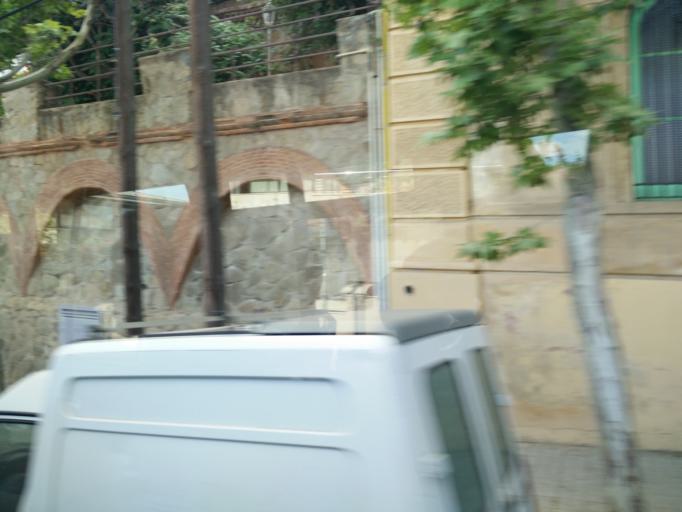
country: ES
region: Catalonia
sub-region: Provincia de Barcelona
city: Sarria-Sant Gervasi
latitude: 41.4157
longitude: 2.1297
